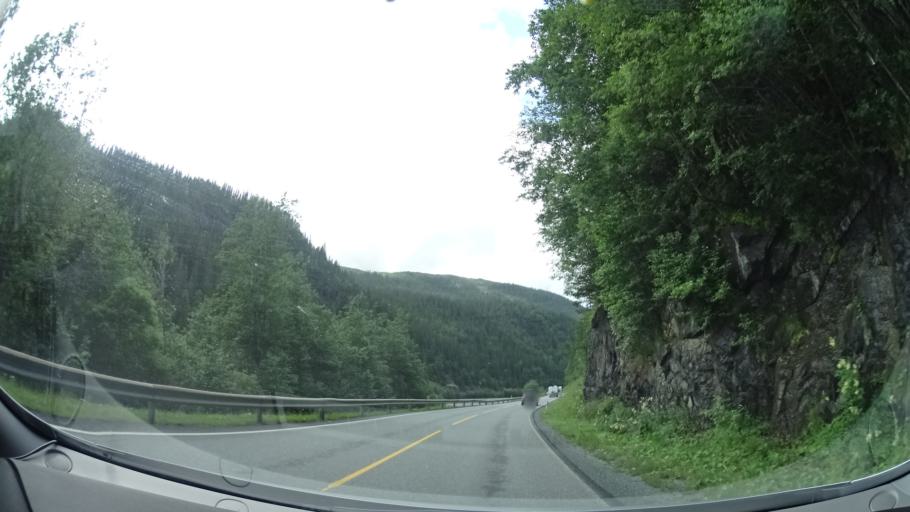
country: NO
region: Nord-Trondelag
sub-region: Meraker
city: Meraker
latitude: 63.4573
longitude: 11.5633
